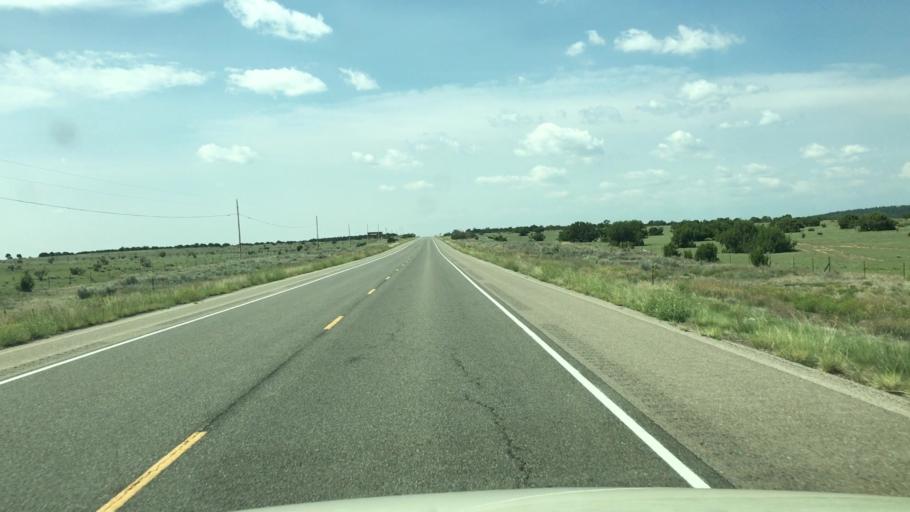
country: US
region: New Mexico
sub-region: Torrance County
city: Moriarty
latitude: 35.0361
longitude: -105.6797
